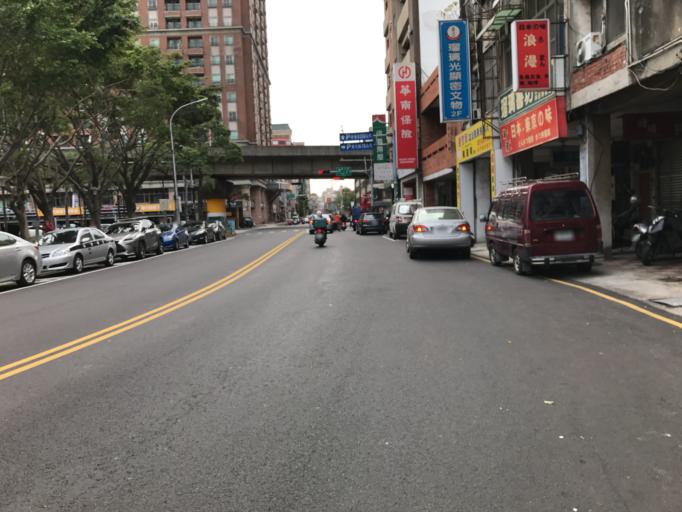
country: TW
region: Taiwan
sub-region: Hsinchu
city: Hsinchu
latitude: 24.8085
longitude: 120.9729
